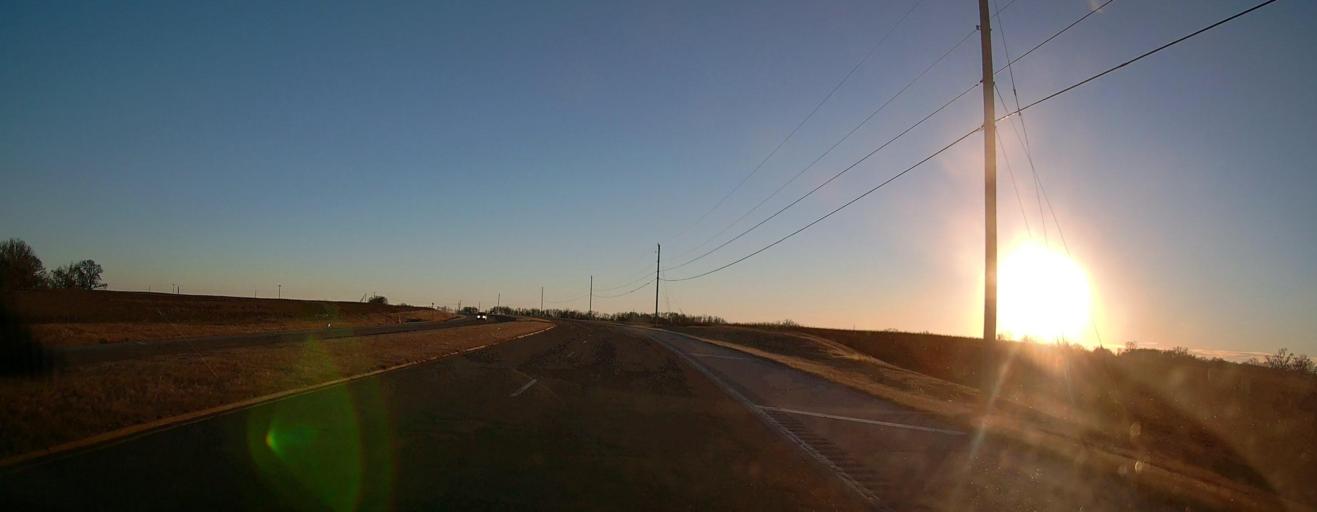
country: US
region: Tennessee
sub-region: Shelby County
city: Millington
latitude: 35.3109
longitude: -89.8805
